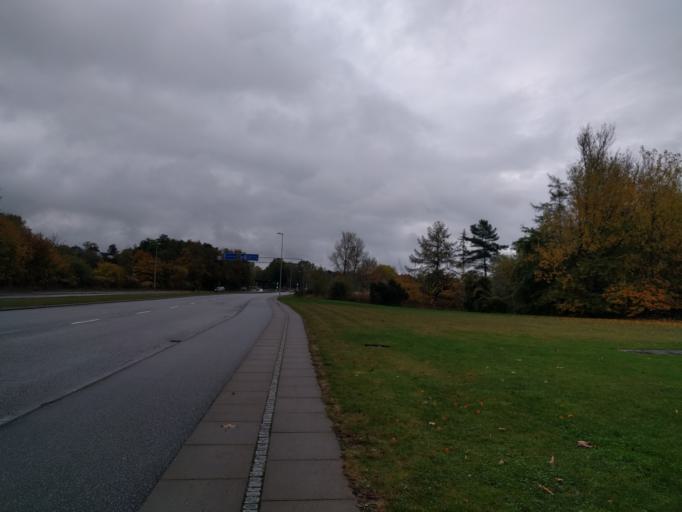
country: DK
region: South Denmark
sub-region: Fredericia Kommune
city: Fredericia
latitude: 55.5606
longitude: 9.7352
